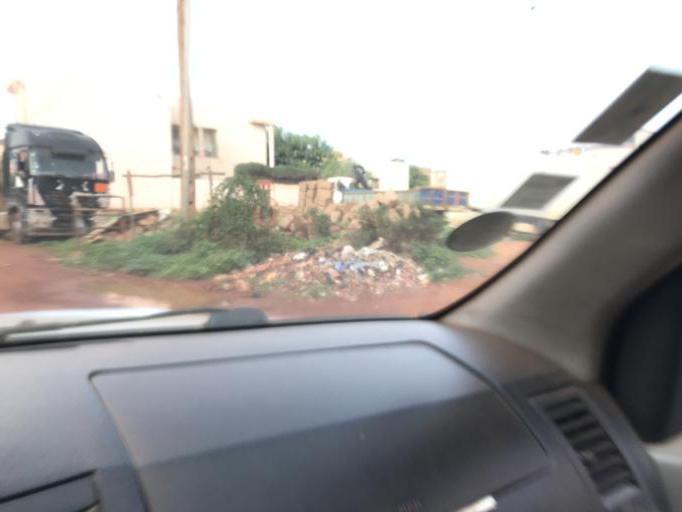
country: ML
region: Bamako
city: Bamako
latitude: 12.5846
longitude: -8.0067
